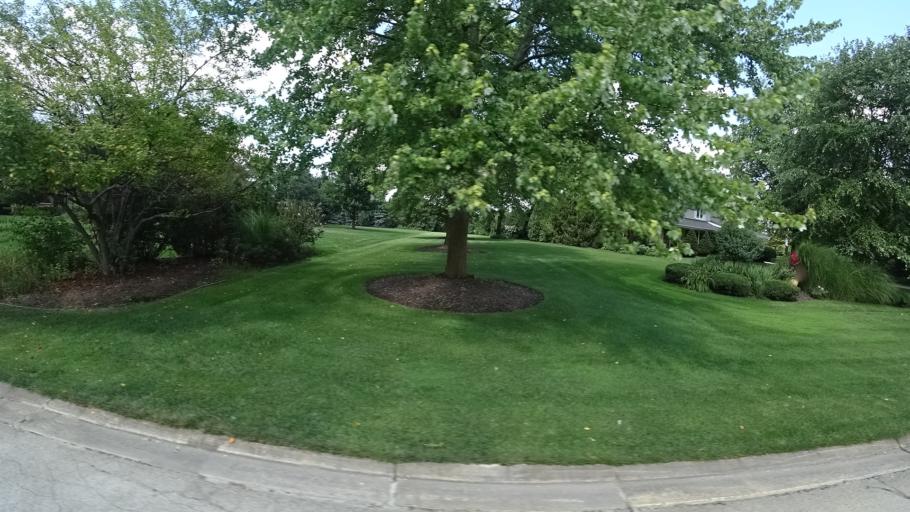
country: US
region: Illinois
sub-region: Cook County
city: Orland Park
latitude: 41.6265
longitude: -87.8218
